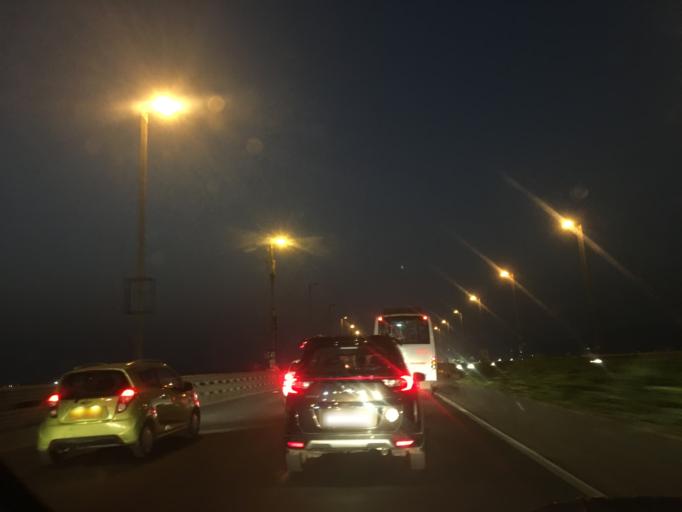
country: IN
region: Maharashtra
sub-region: Thane
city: Airoli
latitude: 19.1506
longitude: 72.9810
